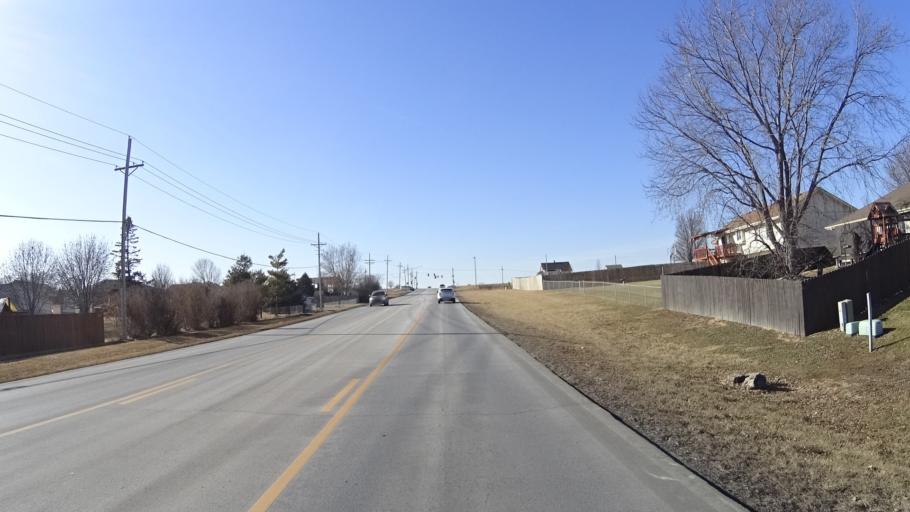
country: US
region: Nebraska
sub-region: Douglas County
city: Bennington
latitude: 41.3067
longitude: -96.1161
